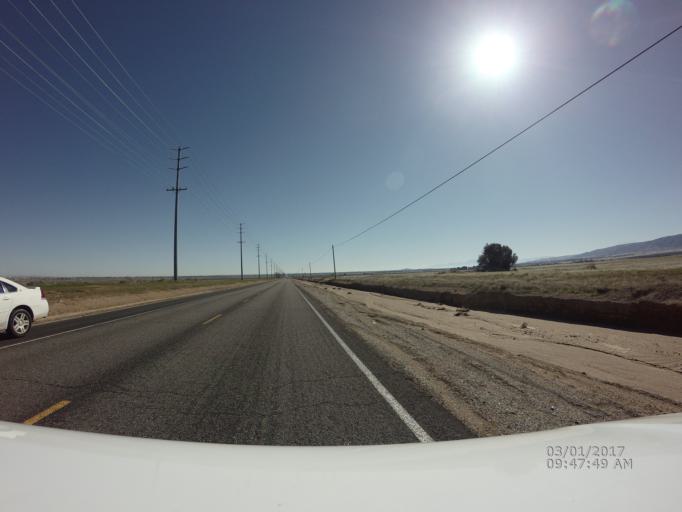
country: US
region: California
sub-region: Los Angeles County
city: Leona Valley
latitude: 34.6747
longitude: -118.2819
